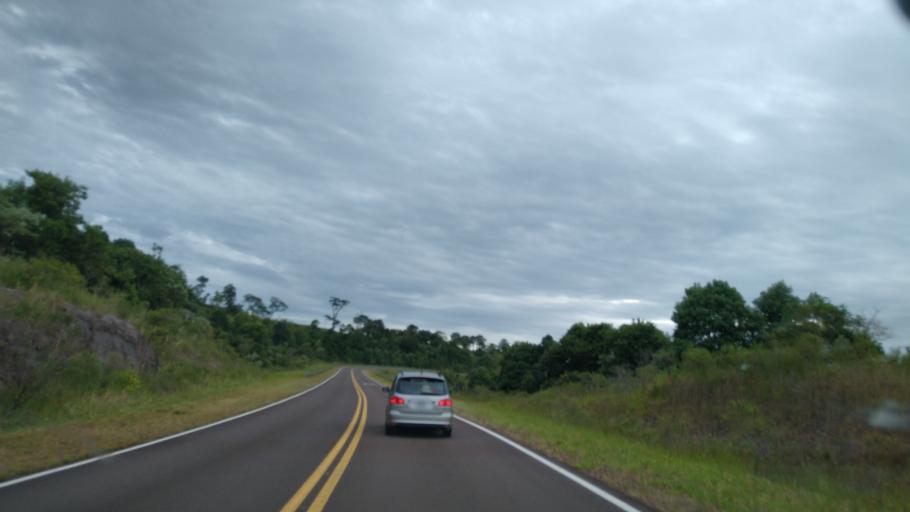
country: AR
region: Misiones
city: Bernardo de Irigoyen
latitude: -26.3853
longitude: -53.7983
